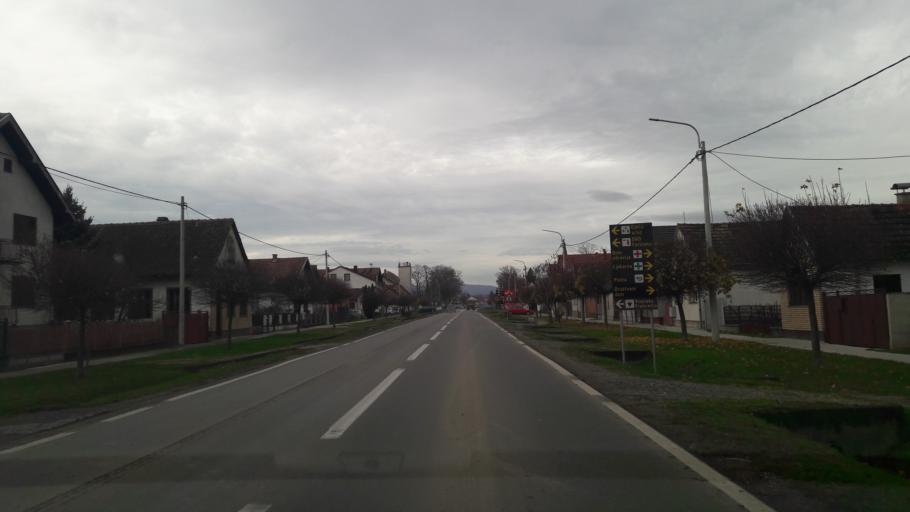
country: HR
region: Osjecko-Baranjska
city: Fericanci
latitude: 45.5238
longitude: 17.9817
